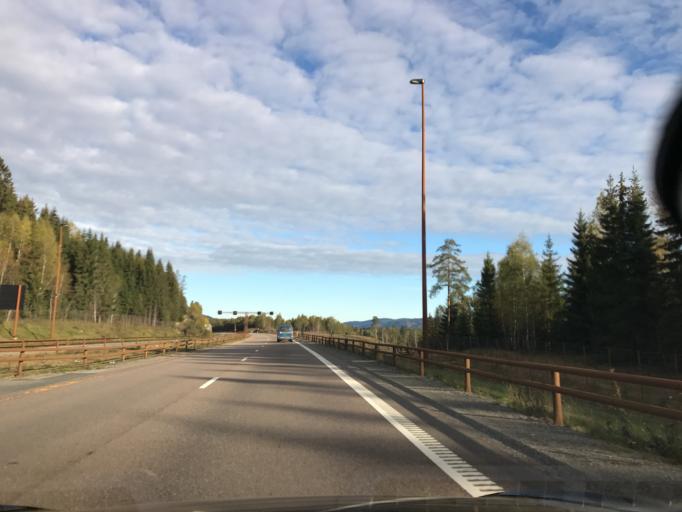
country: NO
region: Akershus
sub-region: Eidsvoll
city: Eidsvoll
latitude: 60.3479
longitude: 11.2090
